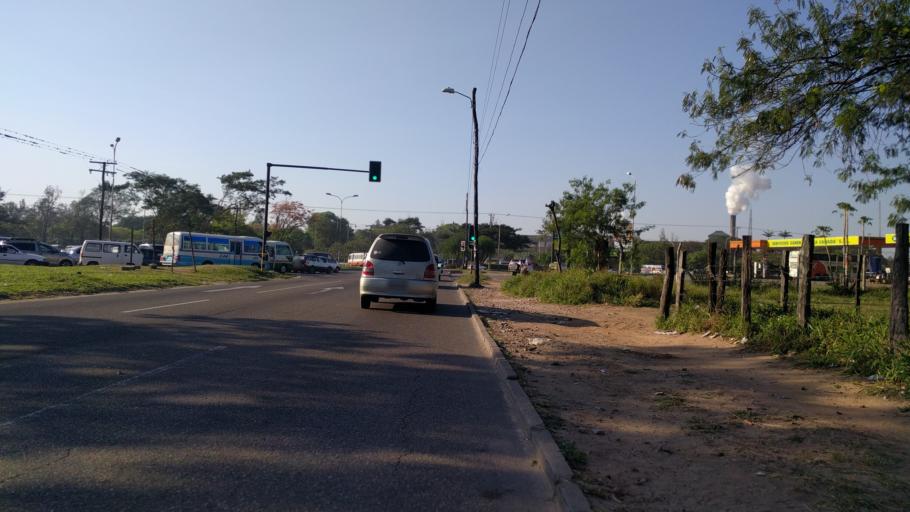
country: BO
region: Santa Cruz
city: Santa Cruz de la Sierra
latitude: -17.8104
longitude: -63.1621
